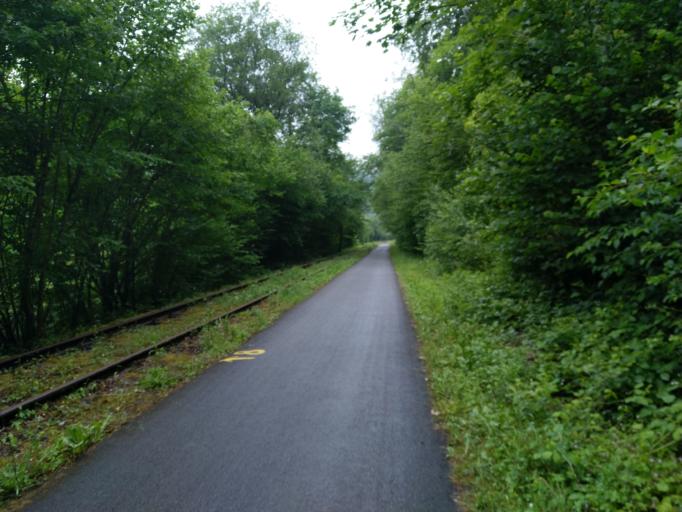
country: BE
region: Wallonia
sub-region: Province de Namur
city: Anhee
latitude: 50.3075
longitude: 4.8321
